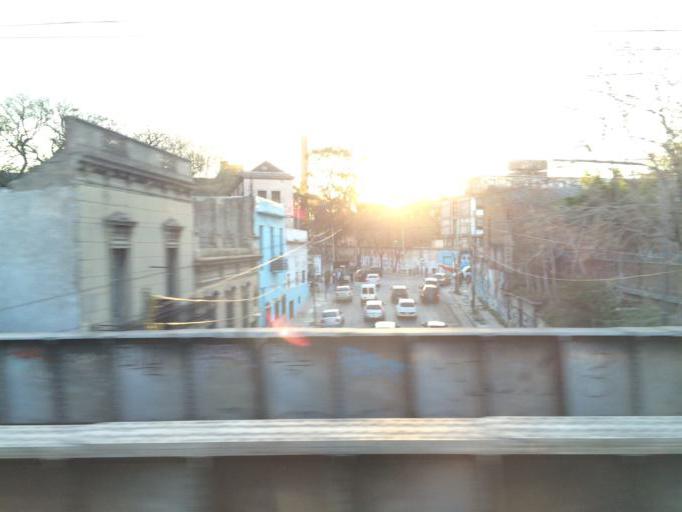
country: AR
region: Buenos Aires
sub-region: Partido de Avellaneda
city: Avellaneda
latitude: -34.6386
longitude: -58.3806
